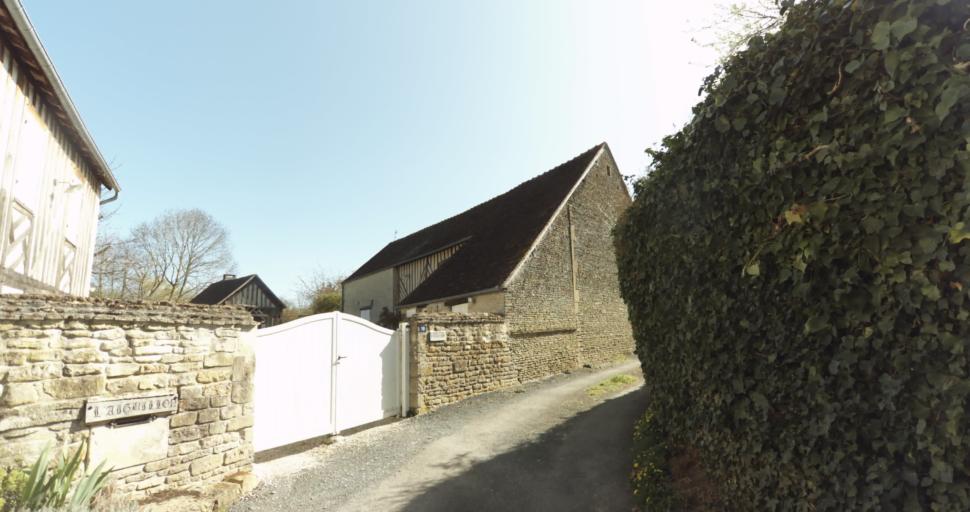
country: FR
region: Lower Normandy
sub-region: Departement du Calvados
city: Saint-Pierre-sur-Dives
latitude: 48.9430
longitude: -0.0037
